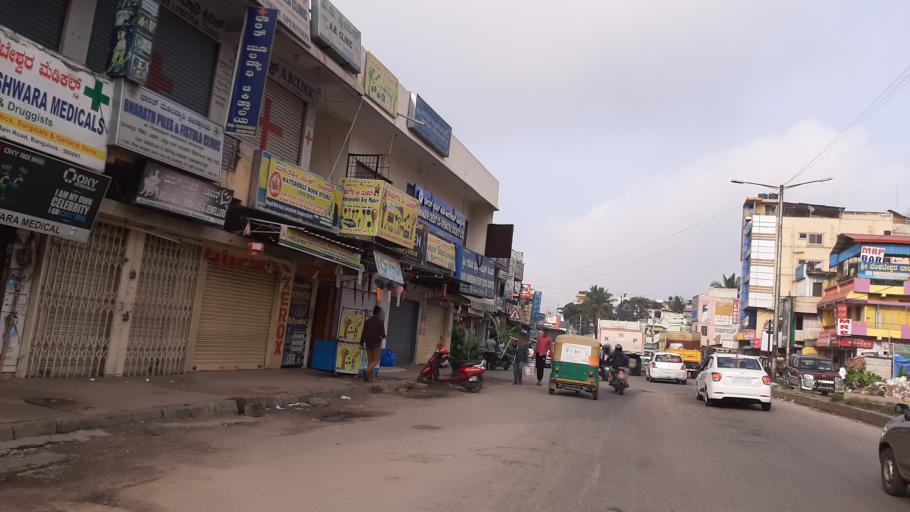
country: IN
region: Karnataka
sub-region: Bangalore Urban
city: Bangalore
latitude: 12.9902
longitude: 77.5039
